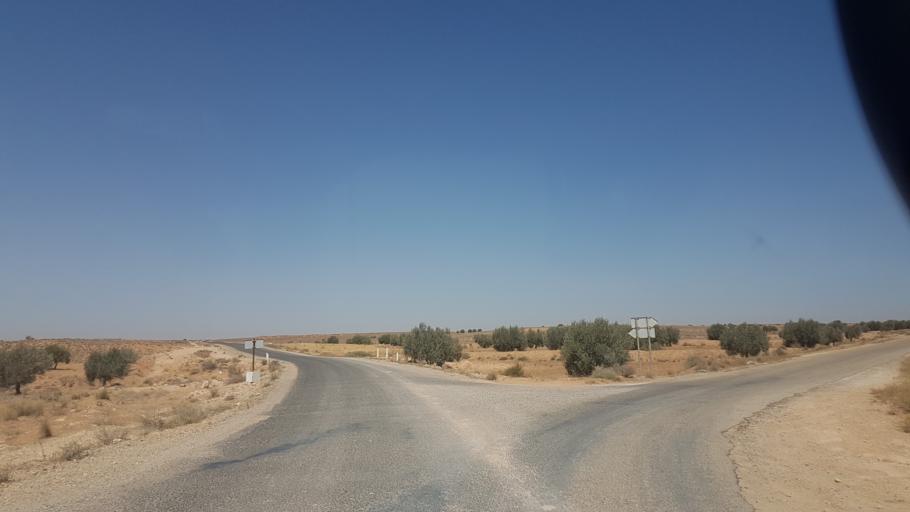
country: TN
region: Madanin
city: Medenine
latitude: 33.3188
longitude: 10.6036
